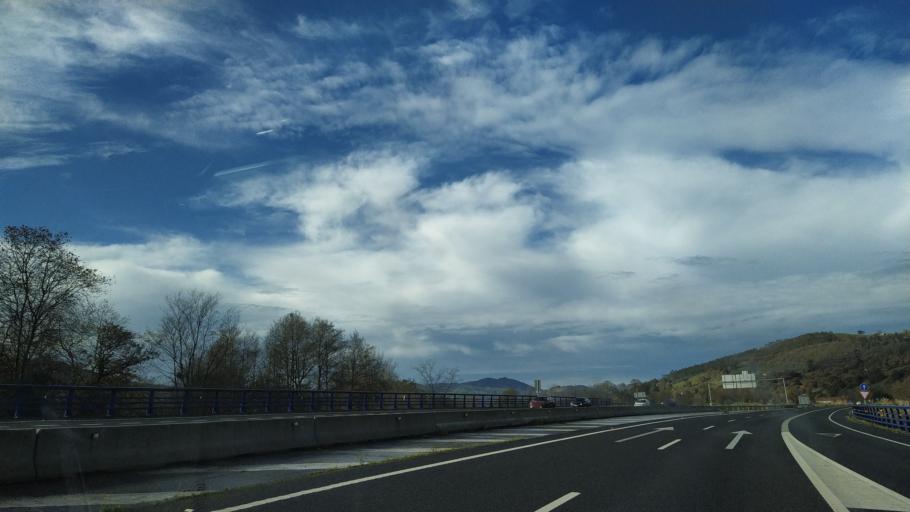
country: ES
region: Cantabria
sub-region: Provincia de Cantabria
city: Santa Maria de Cayon
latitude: 43.3125
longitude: -3.8845
